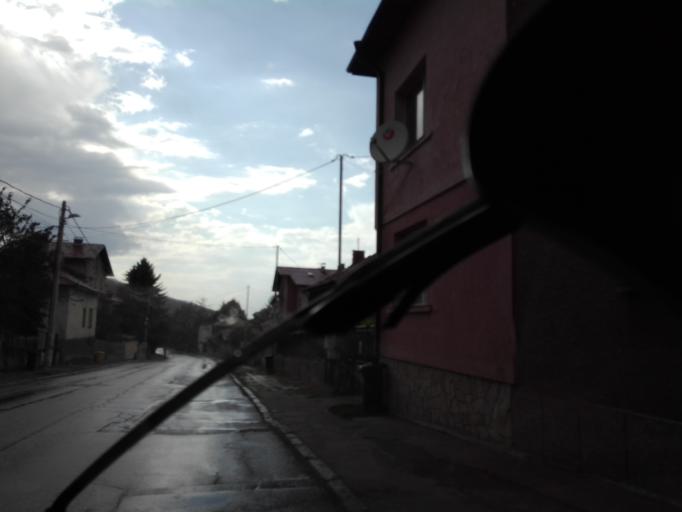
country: BG
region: Sofiya
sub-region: Obshtina Elin Pelin
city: Elin Pelin
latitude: 42.6015
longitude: 23.4825
